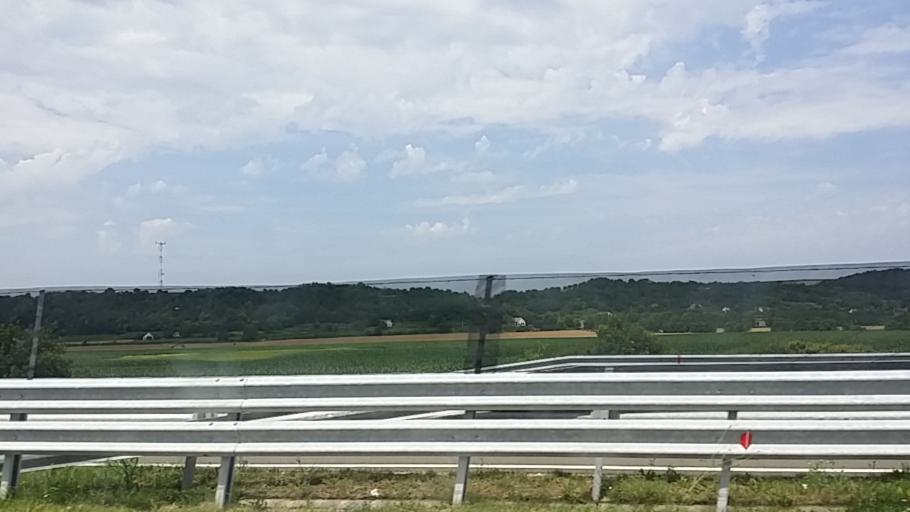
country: HU
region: Tolna
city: Bataszek
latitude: 46.2143
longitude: 18.7034
